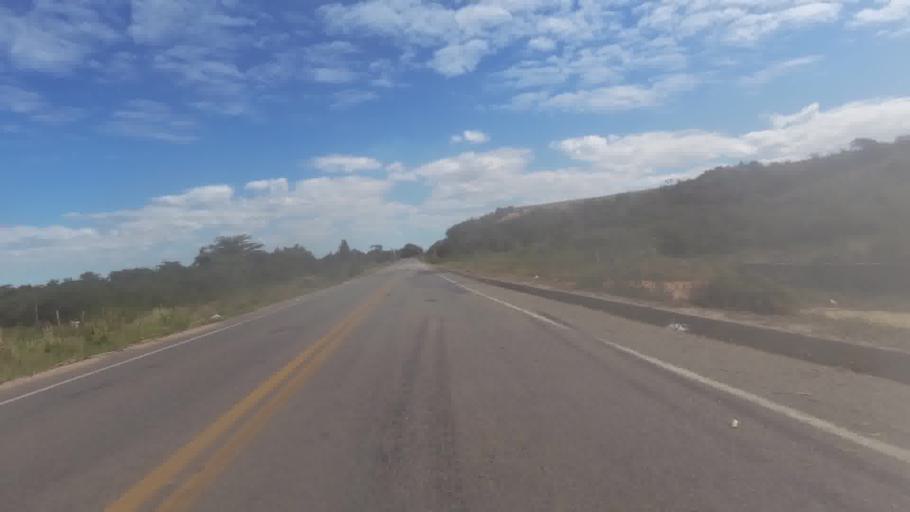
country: BR
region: Espirito Santo
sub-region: Marataizes
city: Marataizes
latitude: -21.1852
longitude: -40.9274
